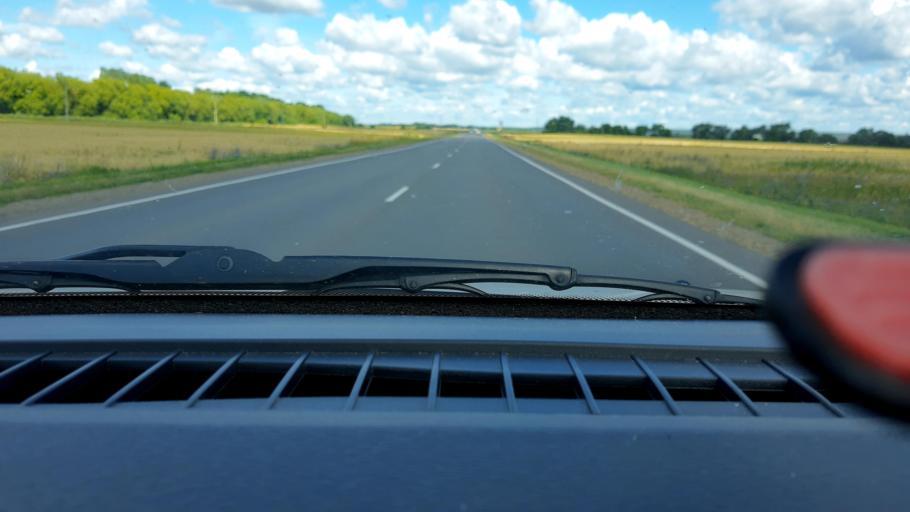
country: RU
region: Nizjnij Novgorod
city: Lesogorsk
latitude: 55.2638
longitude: 43.9721
